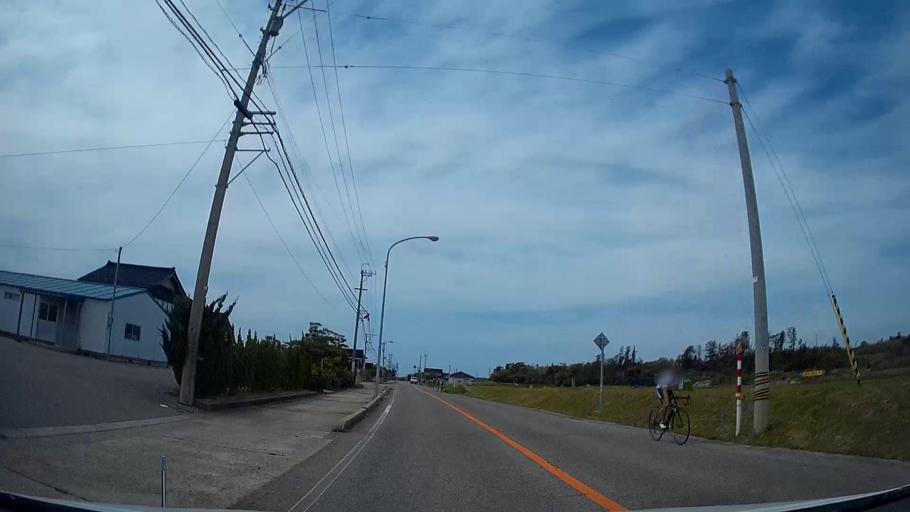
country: JP
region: Ishikawa
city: Hakui
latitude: 37.0349
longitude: 136.7465
